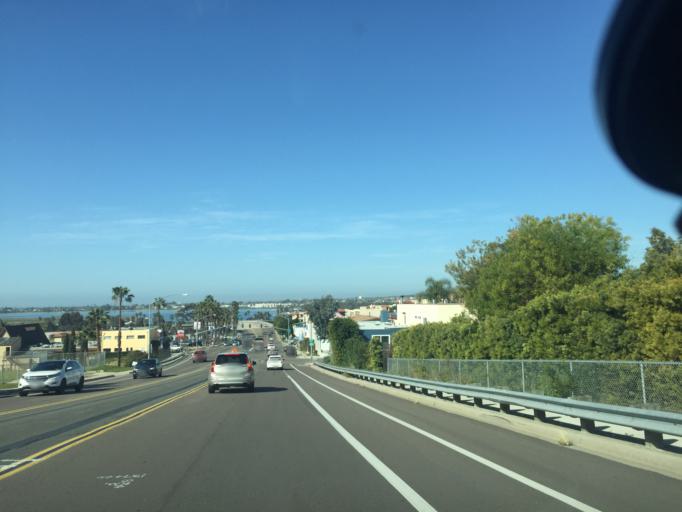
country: US
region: California
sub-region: San Diego County
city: San Diego
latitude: 32.7903
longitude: -117.2012
